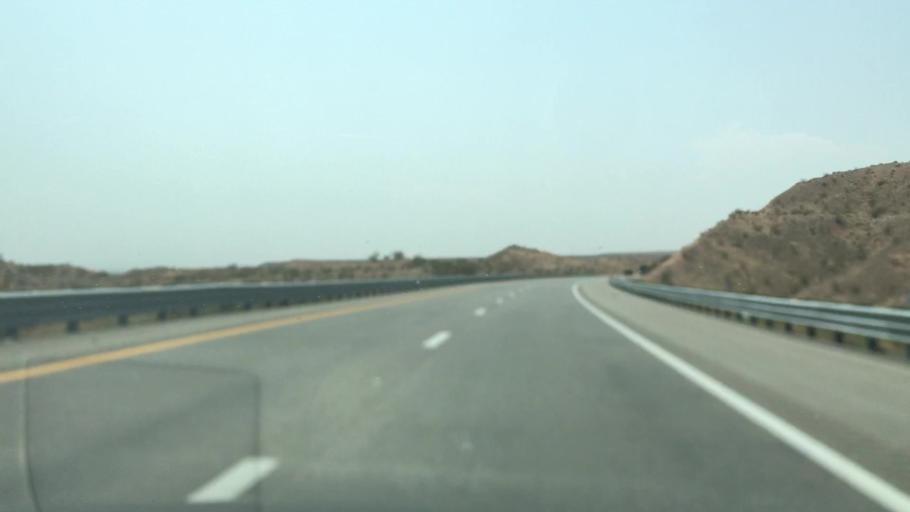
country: US
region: Nevada
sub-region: Clark County
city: Bunkerville
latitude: 36.7651
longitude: -114.1722
